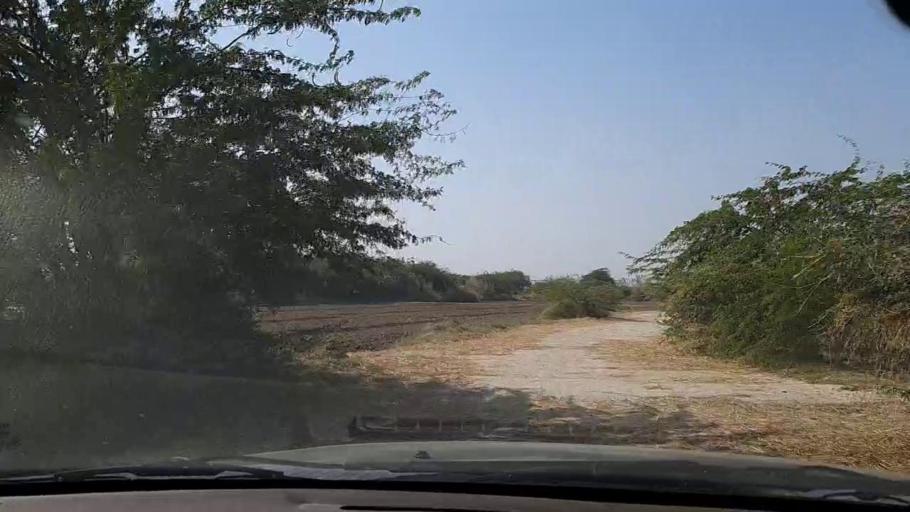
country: PK
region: Sindh
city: Chuhar Jamali
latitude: 24.4278
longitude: 67.8008
